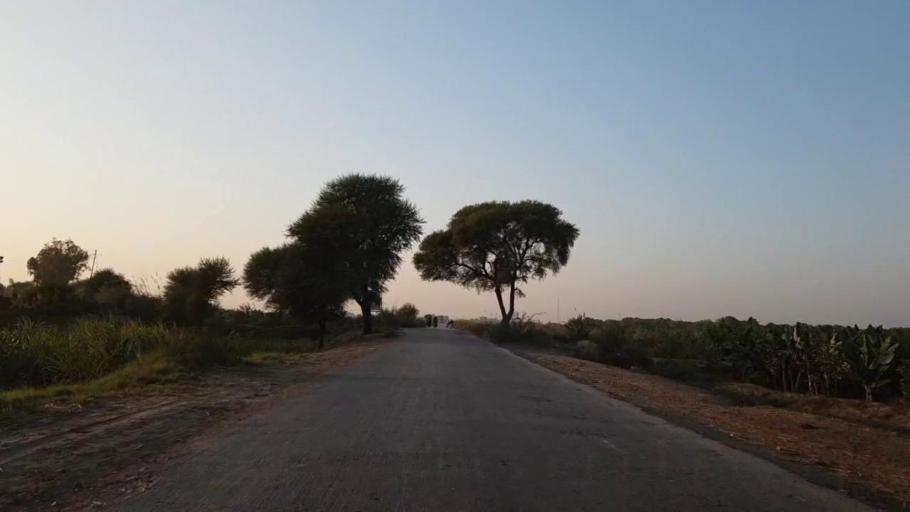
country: PK
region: Sindh
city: Chambar
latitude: 25.2504
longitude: 68.6767
